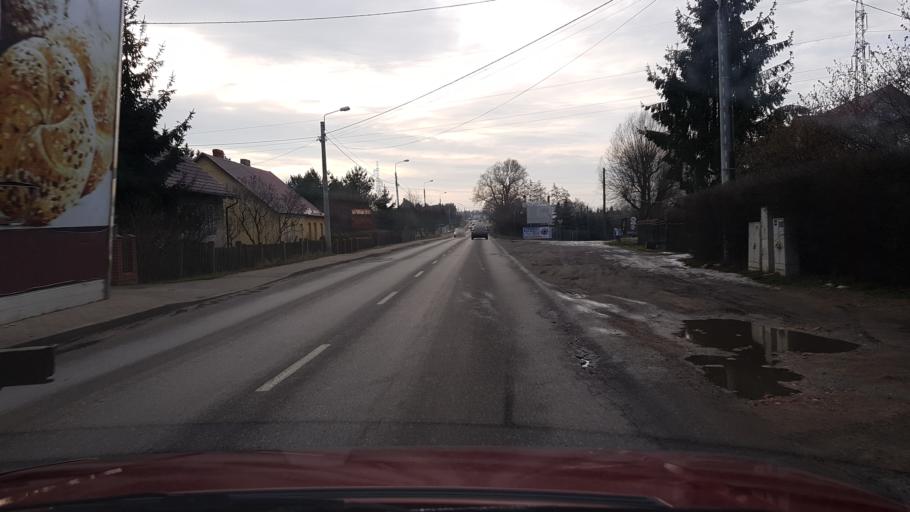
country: PL
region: West Pomeranian Voivodeship
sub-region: Powiat policki
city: Police
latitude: 53.5190
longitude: 14.5680
